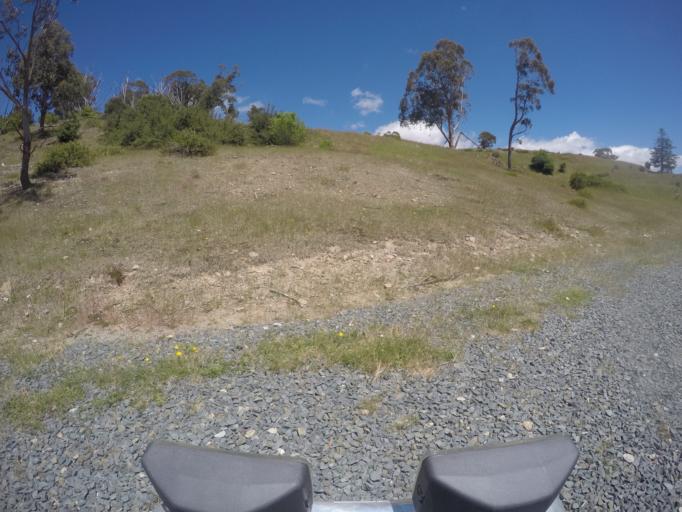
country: AU
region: New South Wales
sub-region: Snowy River
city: Jindabyne
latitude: -35.9378
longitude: 148.3802
